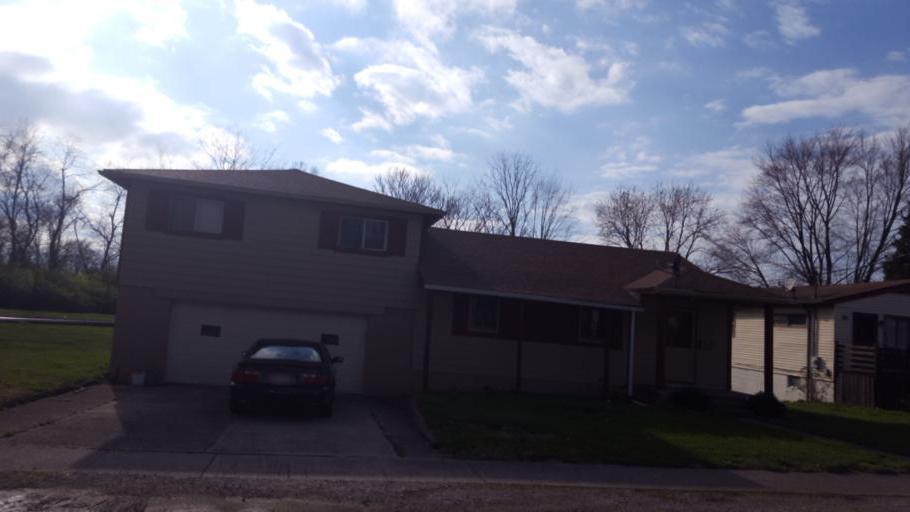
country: US
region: Ohio
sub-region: Delaware County
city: Delaware
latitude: 40.2966
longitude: -83.0558
